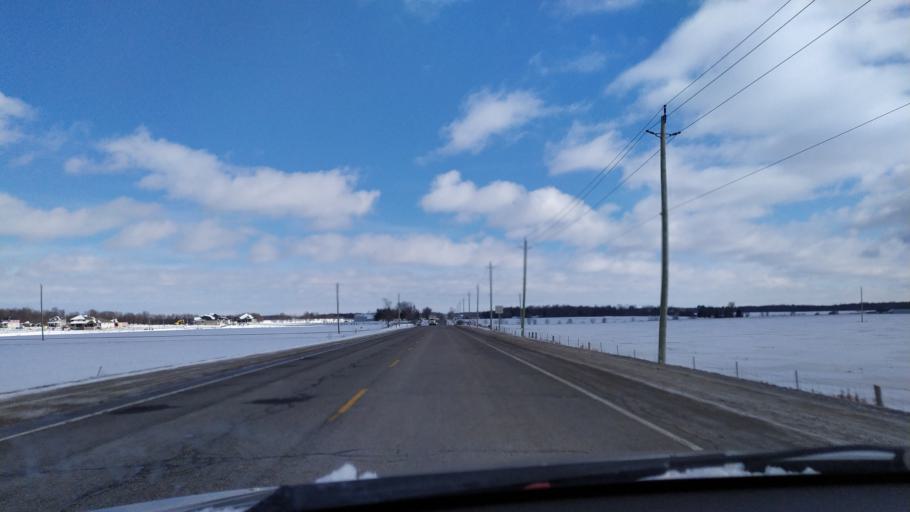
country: CA
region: Ontario
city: Waterloo
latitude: 43.5776
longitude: -80.5780
